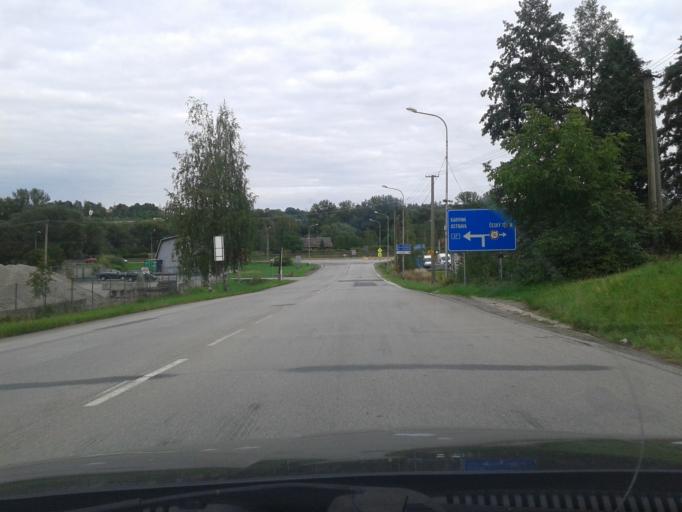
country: CZ
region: Moravskoslezsky
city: Cesky Tesin
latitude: 49.7605
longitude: 18.6087
